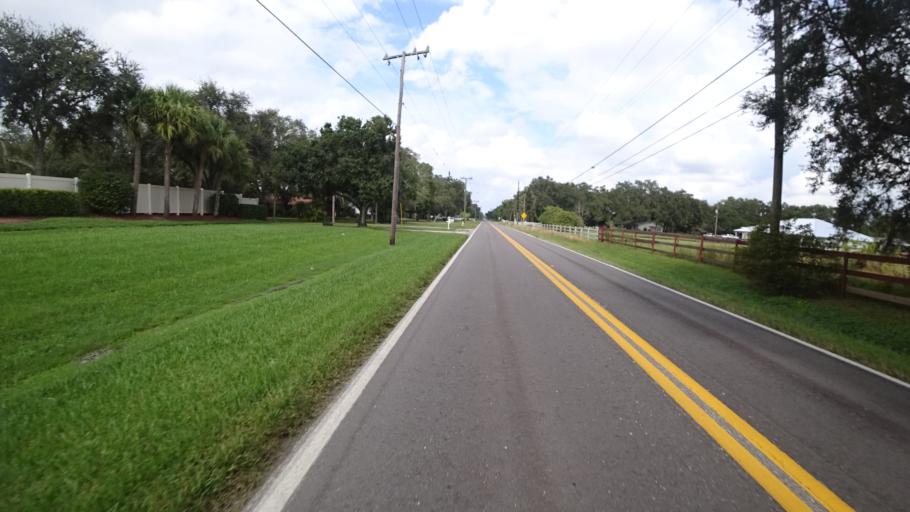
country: US
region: Florida
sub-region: Manatee County
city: Ellenton
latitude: 27.5574
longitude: -82.4788
